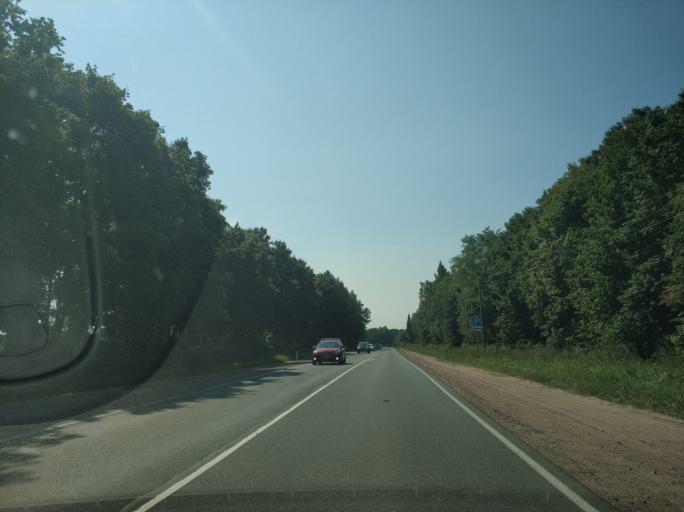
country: RU
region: Leningrad
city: Romanovka
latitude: 60.0642
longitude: 30.7417
